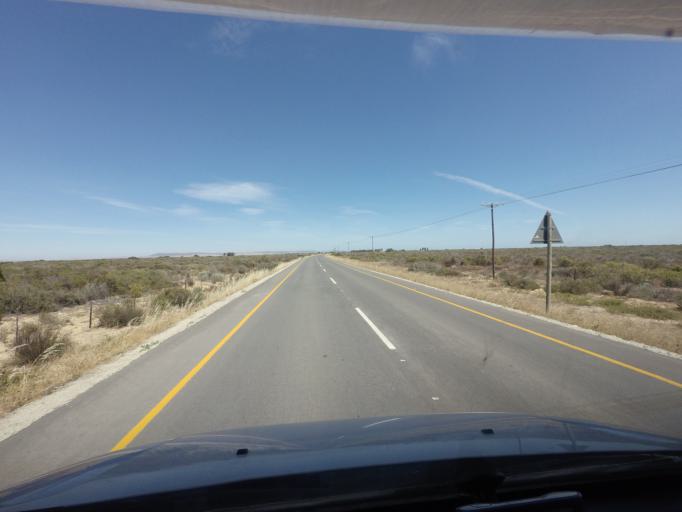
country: ZA
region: Western Cape
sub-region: West Coast District Municipality
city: Vredenburg
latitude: -32.7935
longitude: 18.2322
